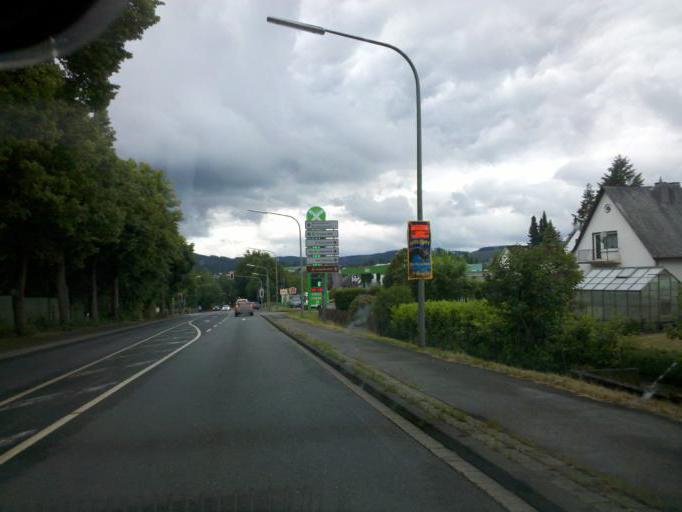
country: DE
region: North Rhine-Westphalia
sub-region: Regierungsbezirk Arnsberg
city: Meschede
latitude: 51.3611
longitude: 8.2872
